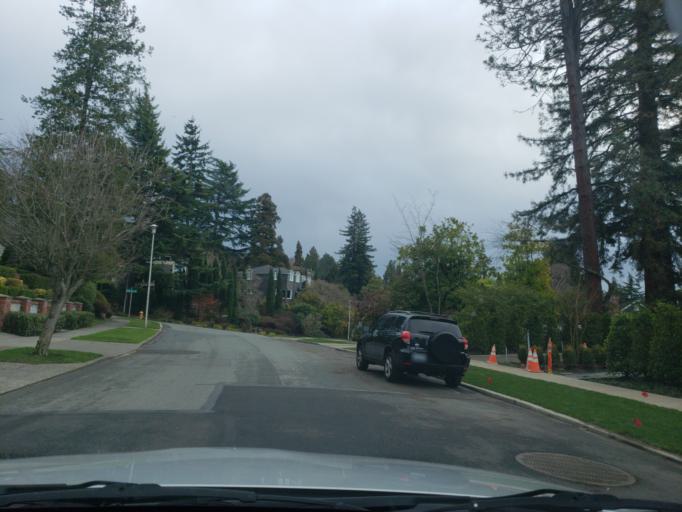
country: US
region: Washington
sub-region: King County
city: Medina
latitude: 47.6546
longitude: -122.2816
